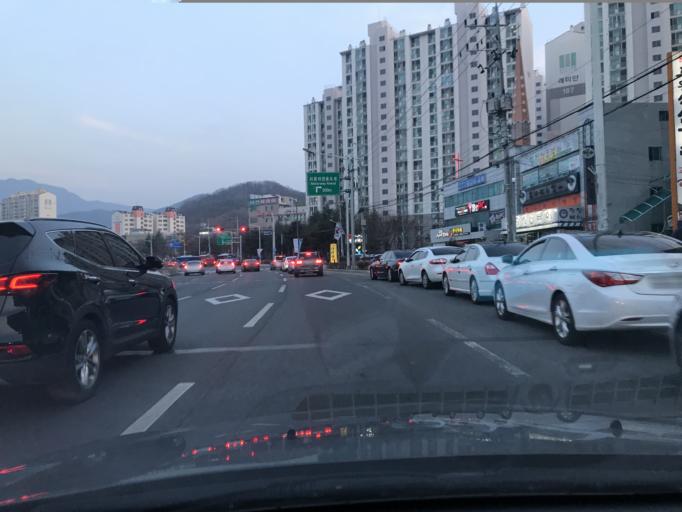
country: KR
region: Daegu
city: Hwawon
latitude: 35.8088
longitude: 128.5177
